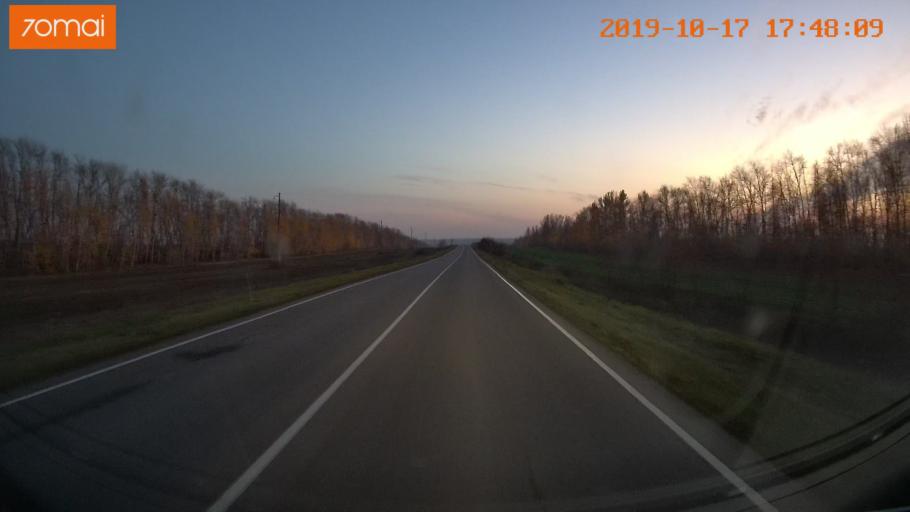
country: RU
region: Tula
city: Yepifan'
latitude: 53.6967
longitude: 38.6962
